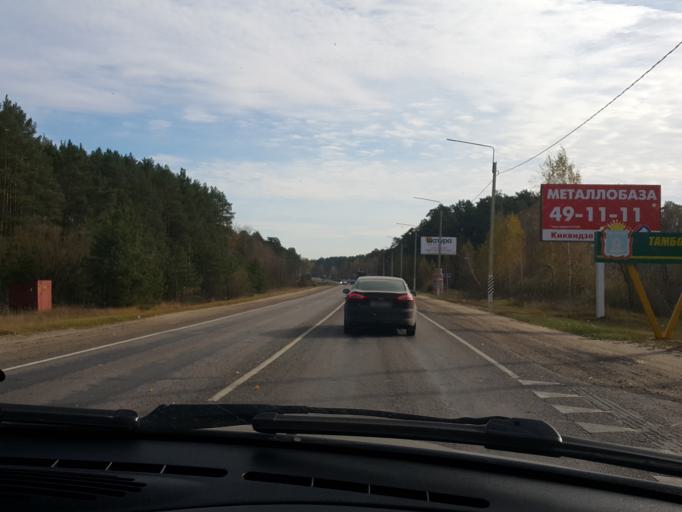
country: RU
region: Tambov
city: Donskoye
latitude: 52.7107
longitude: 41.5269
